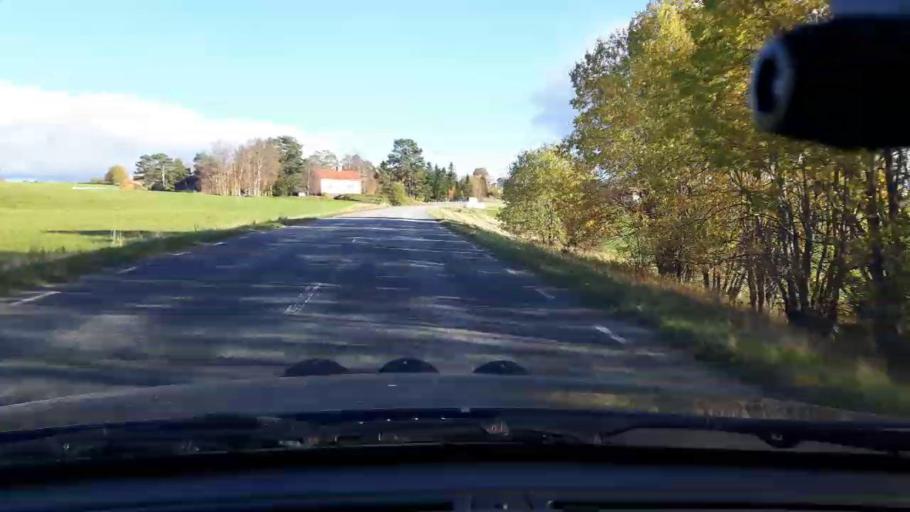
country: SE
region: Jaemtland
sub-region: Bergs Kommun
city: Hoverberg
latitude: 63.0009
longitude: 14.3829
